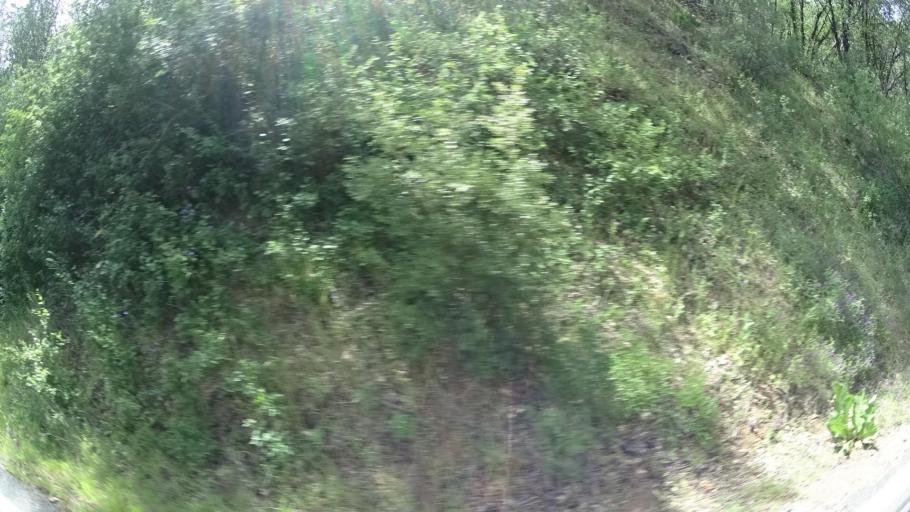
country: US
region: California
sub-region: Lake County
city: Lower Lake
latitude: 38.8939
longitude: -122.6543
